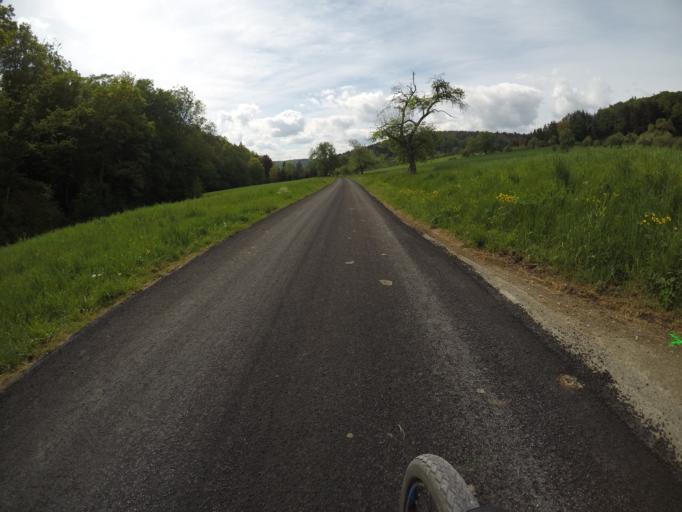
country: DE
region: Baden-Wuerttemberg
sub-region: Tuebingen Region
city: Tuebingen
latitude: 48.5352
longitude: 9.0045
